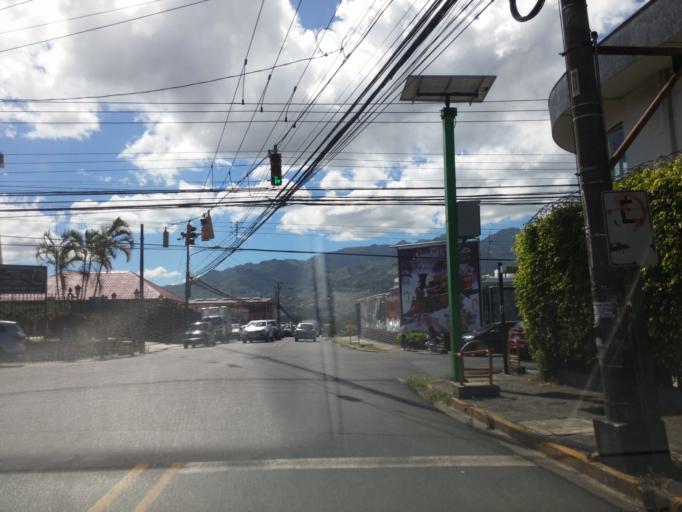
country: CR
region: San Jose
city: San Jose
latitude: 9.9296
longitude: -84.1037
